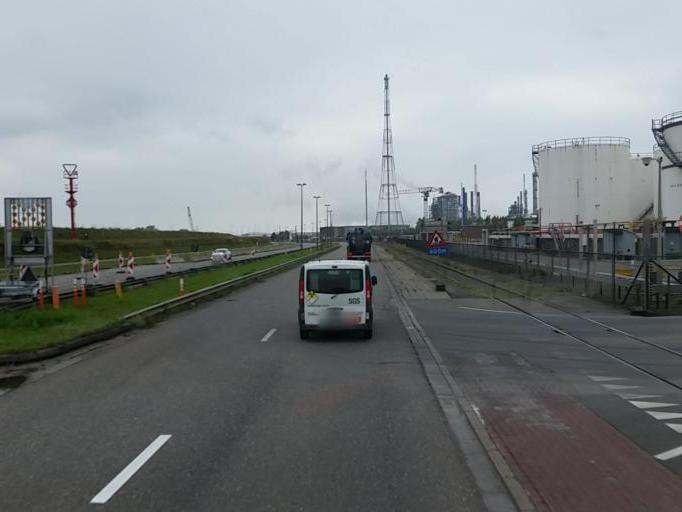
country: BE
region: Flanders
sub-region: Provincie Antwerpen
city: Zwijndrecht
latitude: 51.2514
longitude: 4.3387
